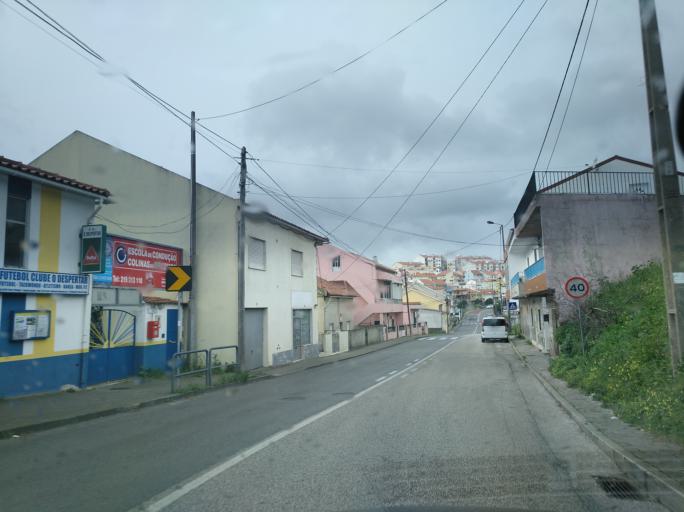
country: PT
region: Lisbon
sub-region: Odivelas
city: Famoes
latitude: 38.7955
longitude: -9.2242
